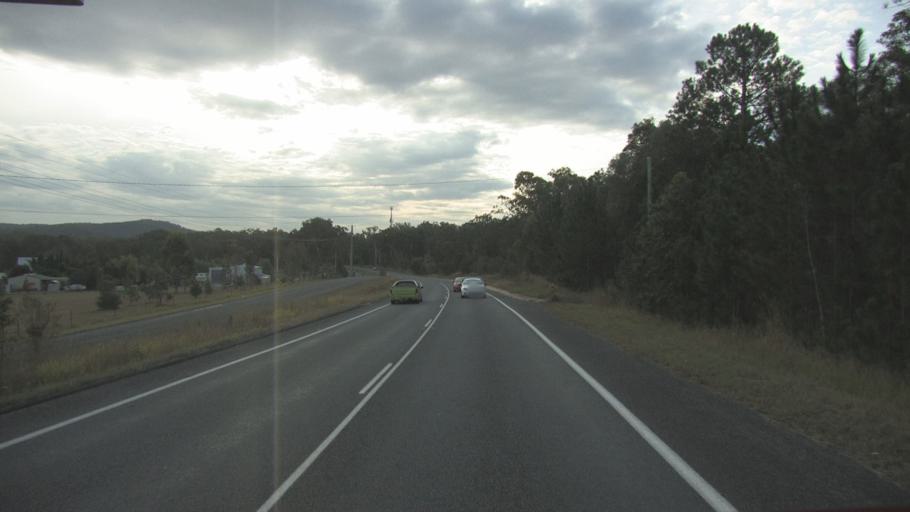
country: AU
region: Queensland
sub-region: Logan
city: Cedar Vale
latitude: -27.8429
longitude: 153.1180
